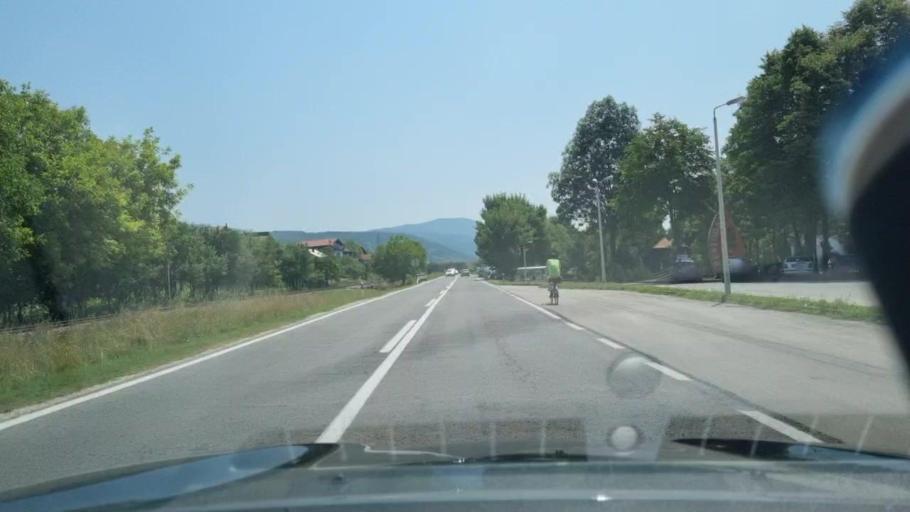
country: BA
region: Federation of Bosnia and Herzegovina
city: Bihac
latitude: 44.8019
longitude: 15.9067
